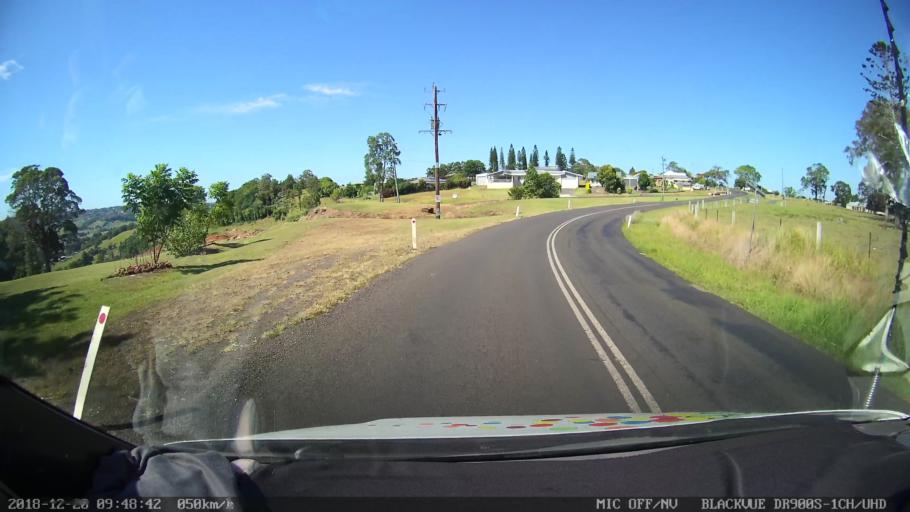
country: AU
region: New South Wales
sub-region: Lismore Municipality
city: Lismore
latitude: -28.7715
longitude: 153.2907
